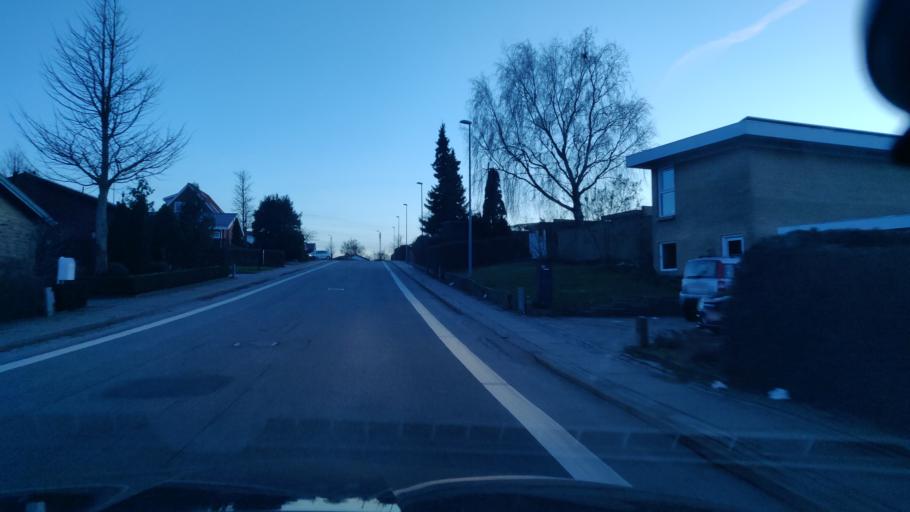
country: DK
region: North Denmark
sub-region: Alborg Kommune
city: Aalborg
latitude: 57.0252
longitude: 9.9327
